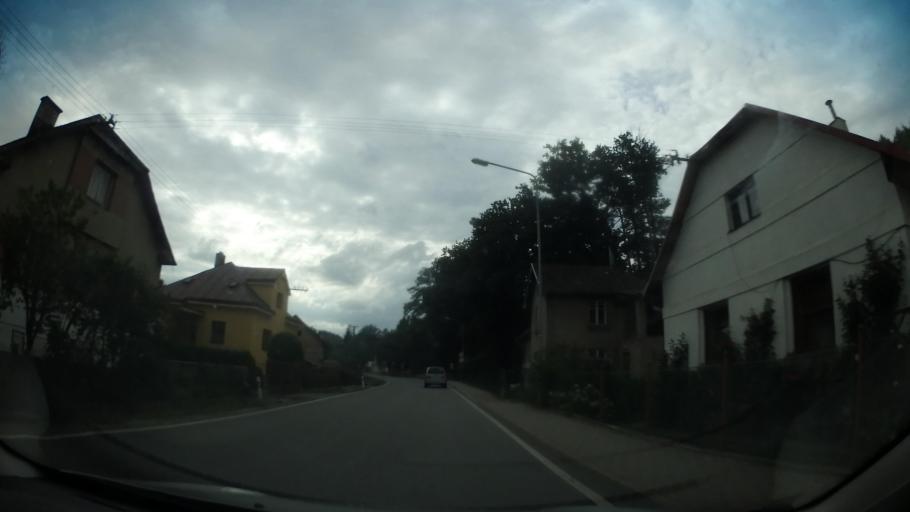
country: CZ
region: Pardubicky
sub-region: Okres Chrudim
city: Nasavrky
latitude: 49.8035
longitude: 15.7445
